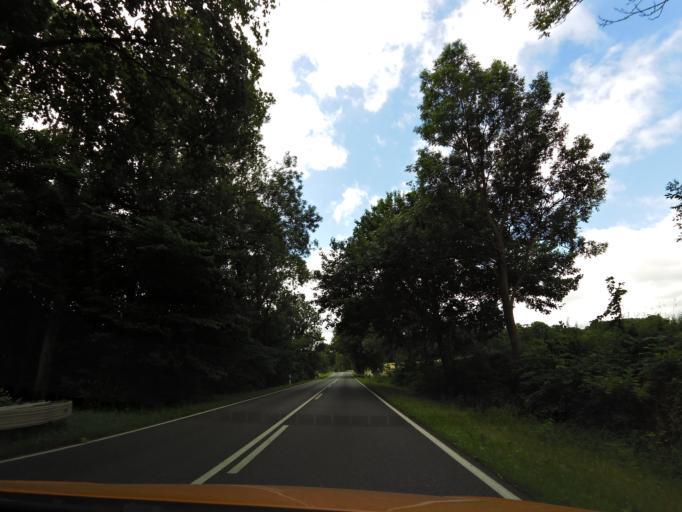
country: DE
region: Mecklenburg-Vorpommern
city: Krakow am See
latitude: 53.6910
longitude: 12.2691
